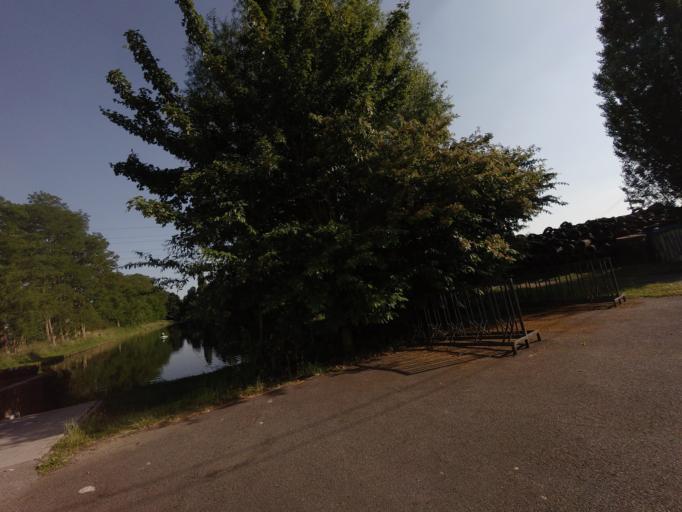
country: BE
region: Flanders
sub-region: Provincie Antwerpen
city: Kontich
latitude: 51.1024
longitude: 4.4645
